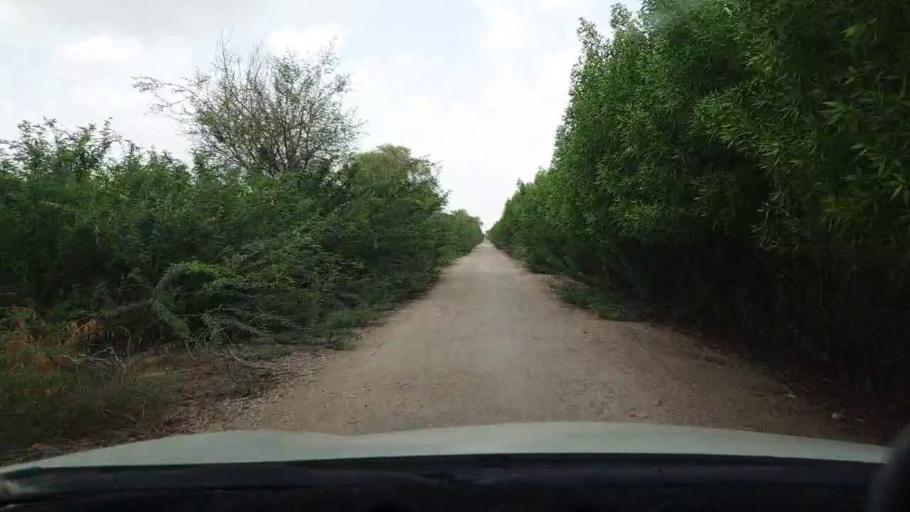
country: PK
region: Sindh
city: Kadhan
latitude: 24.3603
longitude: 68.9603
